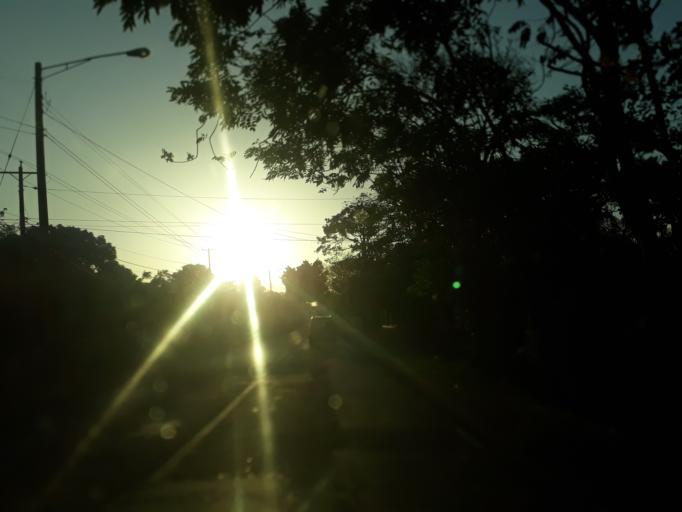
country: NI
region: Masaya
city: Niquinohomo
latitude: 11.9075
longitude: -86.0862
